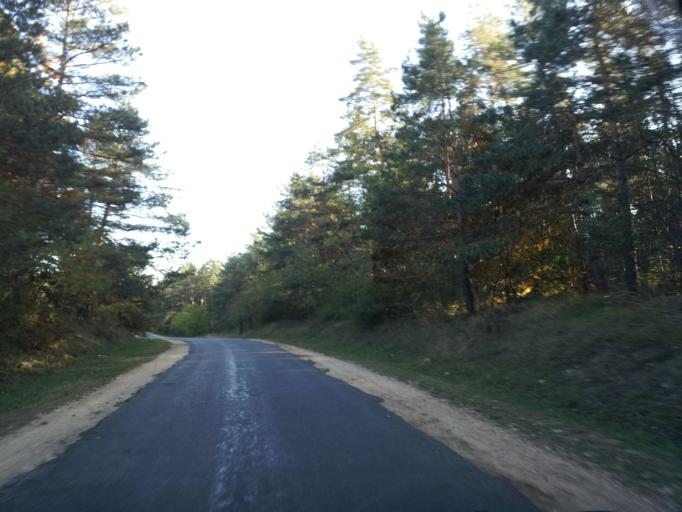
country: HU
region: Gyor-Moson-Sopron
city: Bakonyszentlaszlo
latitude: 47.3766
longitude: 17.8094
